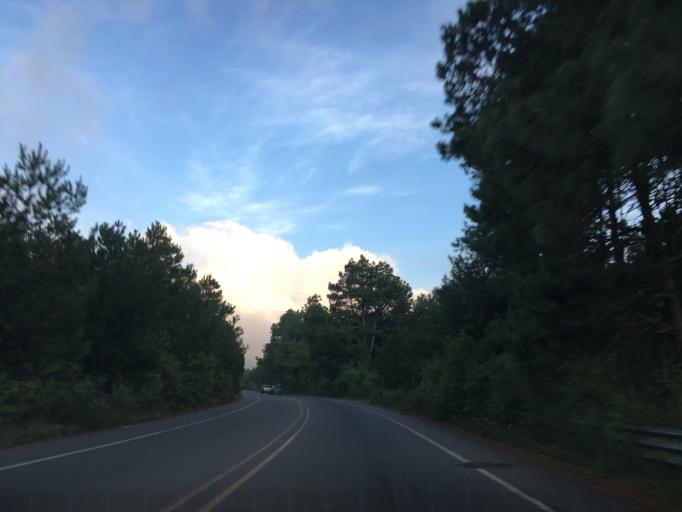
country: MX
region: Michoacan
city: Angahuan
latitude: 19.5682
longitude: -102.2532
